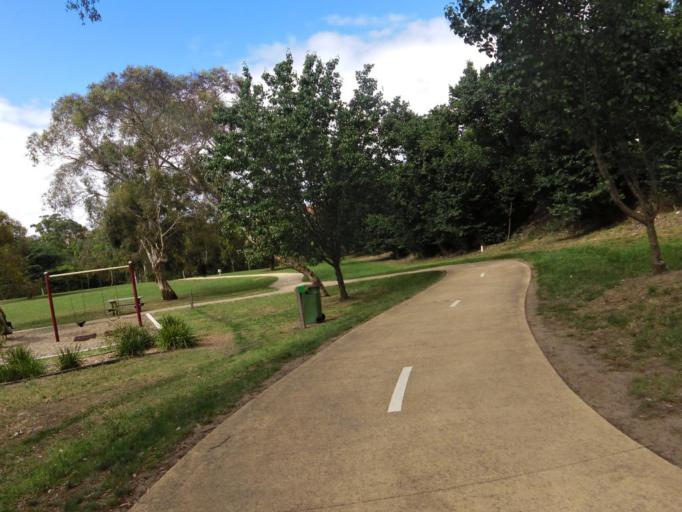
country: AU
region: Victoria
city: Alphington
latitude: -37.7781
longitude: 145.0370
